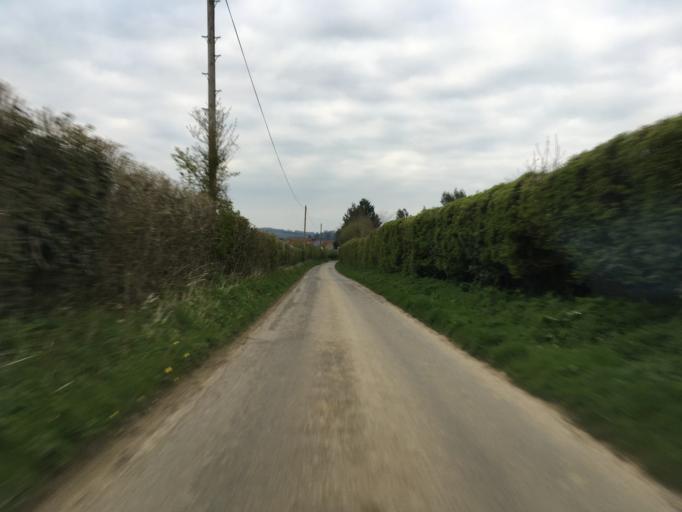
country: GB
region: England
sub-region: Gloucestershire
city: Wotton-under-Edge
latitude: 51.6003
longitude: -2.3373
